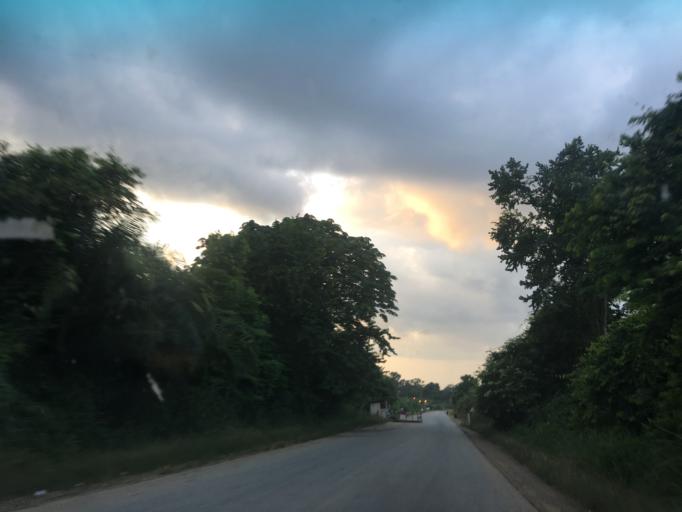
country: GH
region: Western
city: Bibiani
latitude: 6.7471
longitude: -2.5042
